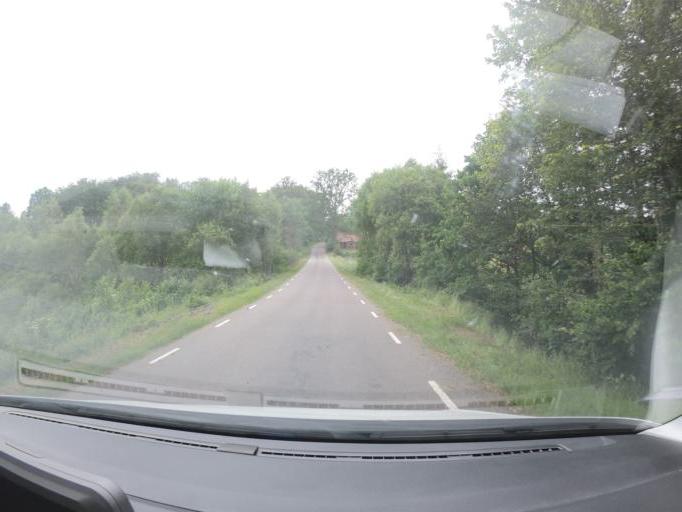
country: SE
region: Skane
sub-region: Perstorps Kommun
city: Perstorp
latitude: 56.1475
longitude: 13.5016
